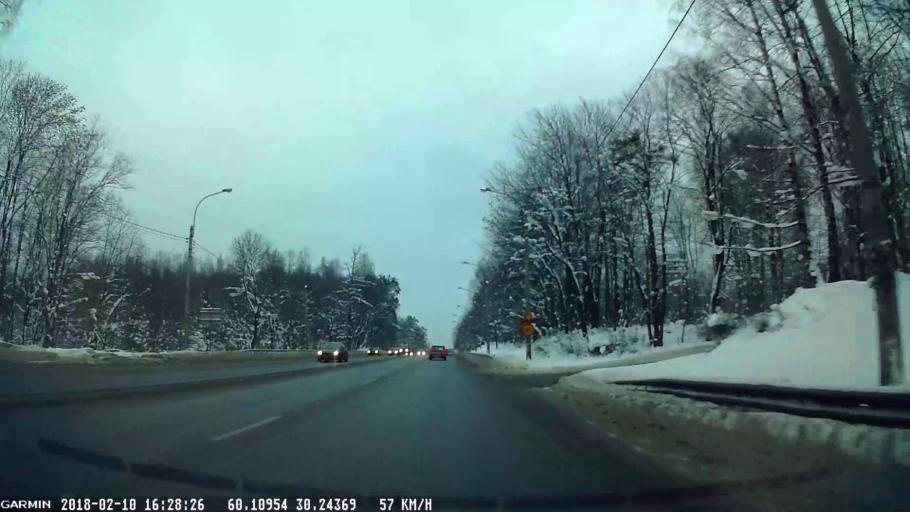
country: RU
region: St.-Petersburg
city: Levashovo
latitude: 60.1099
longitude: 30.2434
